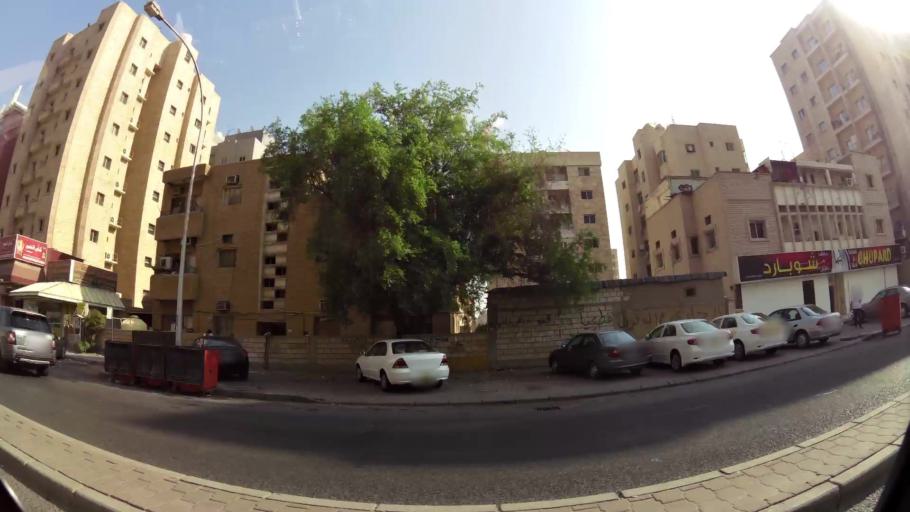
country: KW
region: Muhafazat Hawalli
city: Hawalli
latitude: 29.3346
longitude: 48.0080
